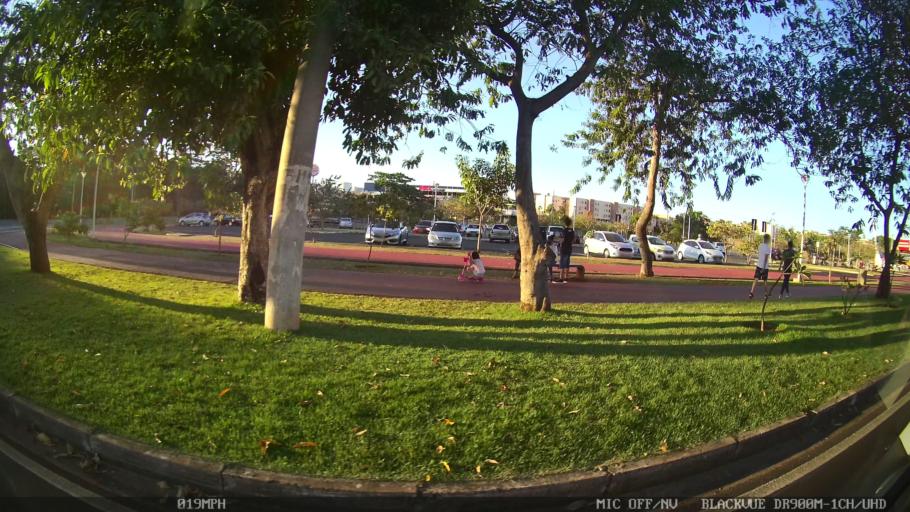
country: BR
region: Sao Paulo
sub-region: Sao Jose Do Rio Preto
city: Sao Jose do Rio Preto
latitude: -20.7839
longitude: -49.3797
